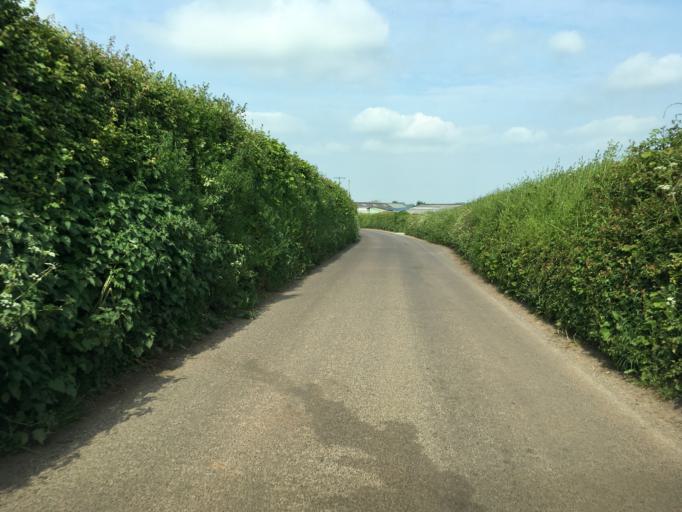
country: GB
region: England
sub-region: North Somerset
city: Brockley
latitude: 51.4082
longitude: -2.7523
